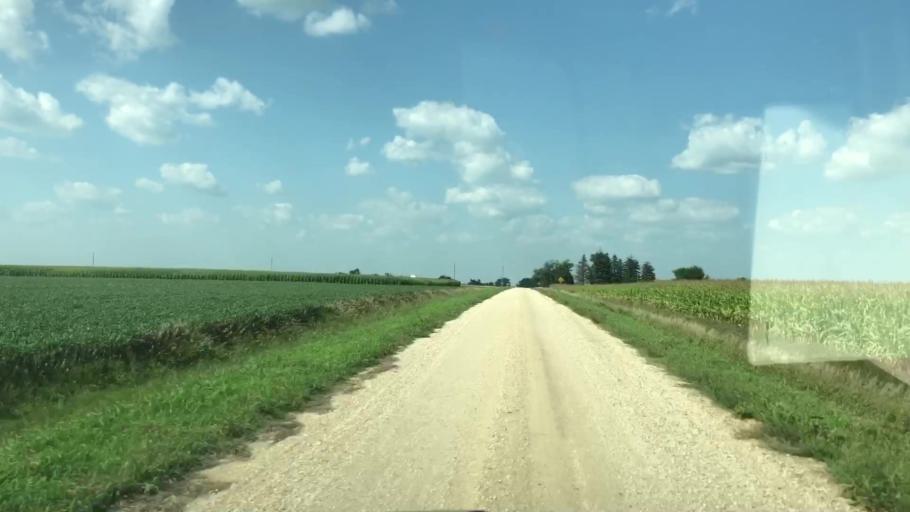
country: US
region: Iowa
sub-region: O'Brien County
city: Sheldon
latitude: 43.1828
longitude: -95.7824
